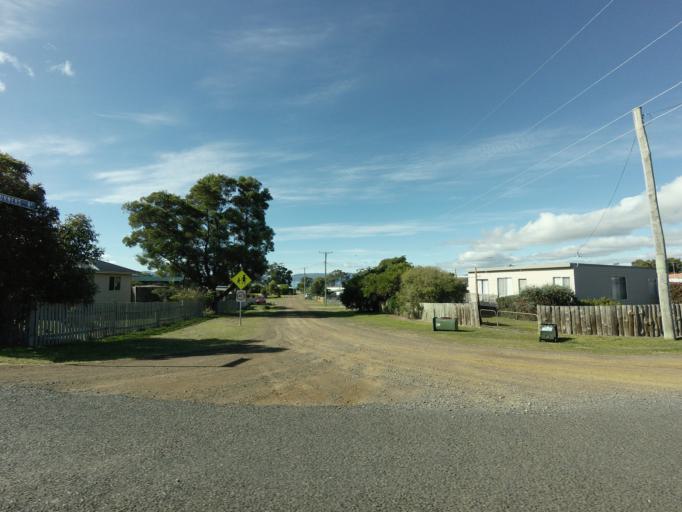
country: AU
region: Tasmania
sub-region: Clarence
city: Sandford
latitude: -42.9943
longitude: 147.7113
